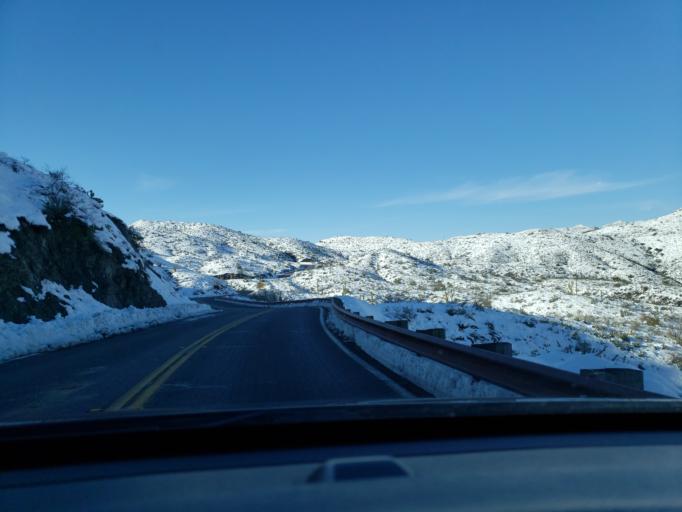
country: US
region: Arizona
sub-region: Maricopa County
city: Carefree
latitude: 33.8884
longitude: -111.8192
